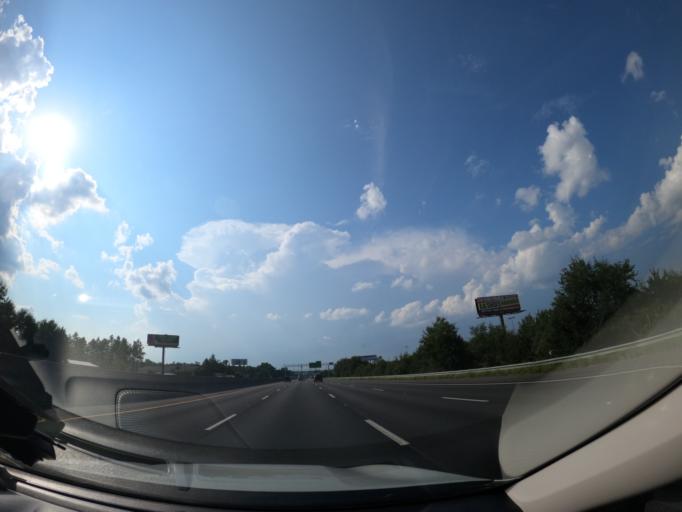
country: US
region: Georgia
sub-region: Columbia County
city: Martinez
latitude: 33.4575
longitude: -82.0768
